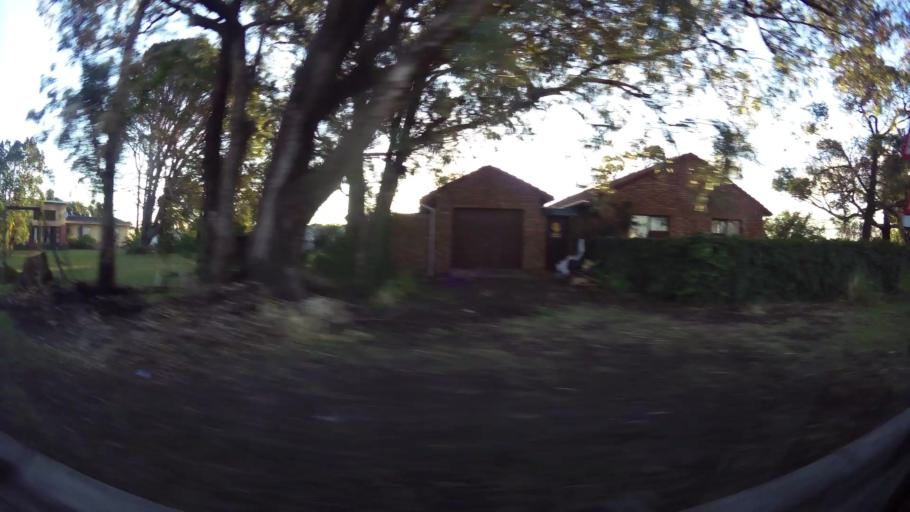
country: ZA
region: Eastern Cape
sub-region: Nelson Mandela Bay Metropolitan Municipality
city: Port Elizabeth
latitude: -33.9752
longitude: 25.5266
